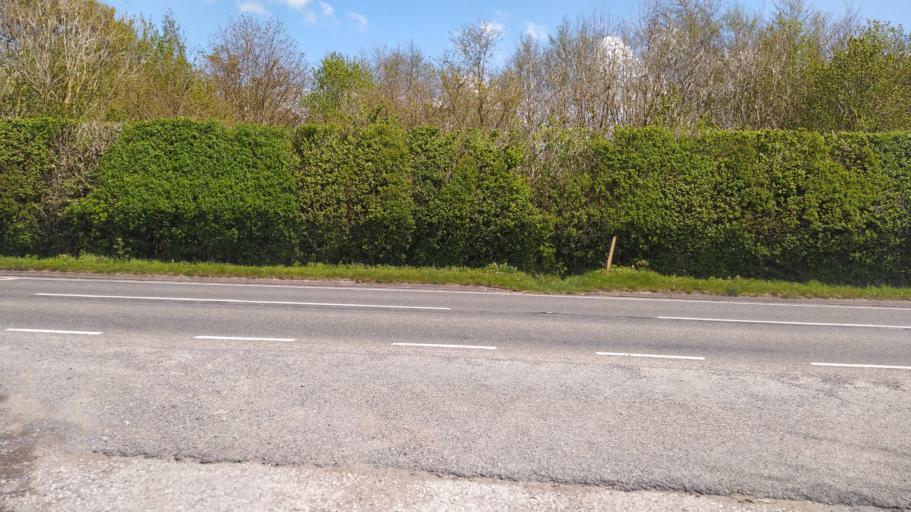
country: GB
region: England
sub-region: Somerset
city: Frome
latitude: 51.1867
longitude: -2.3159
